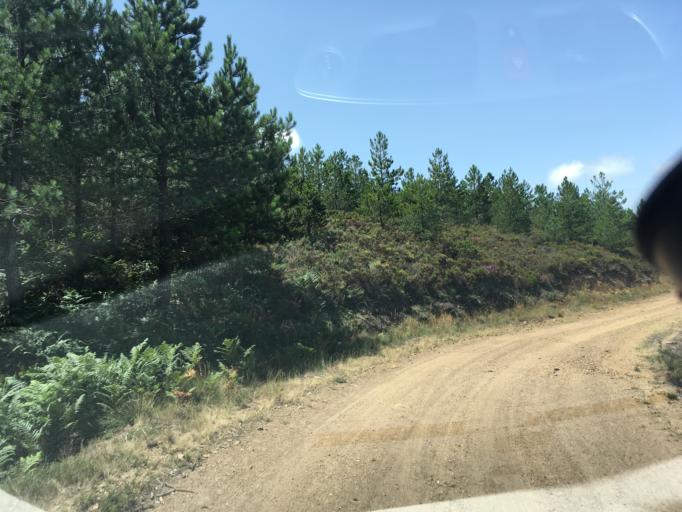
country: PT
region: Porto
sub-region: Baiao
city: Valadares
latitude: 41.2691
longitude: -7.9511
